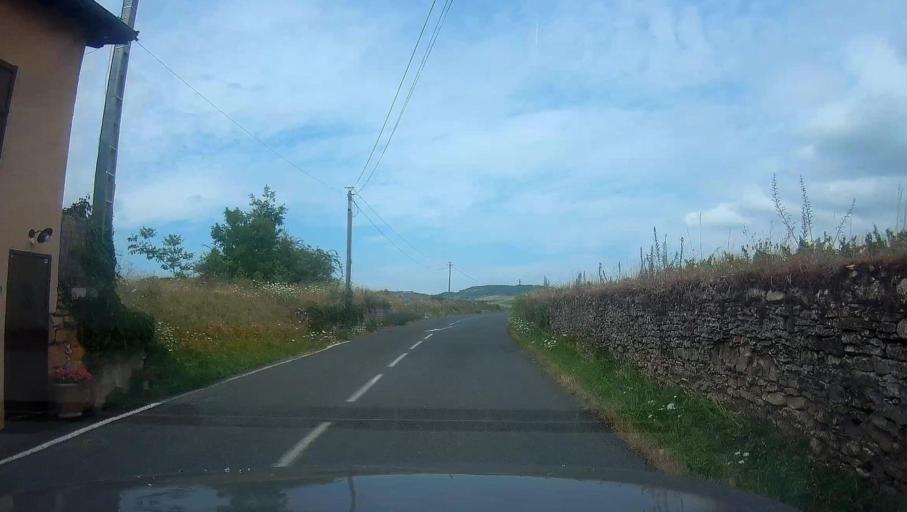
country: FR
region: Rhone-Alpes
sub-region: Departement du Rhone
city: Theize
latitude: 45.9193
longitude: 4.6195
